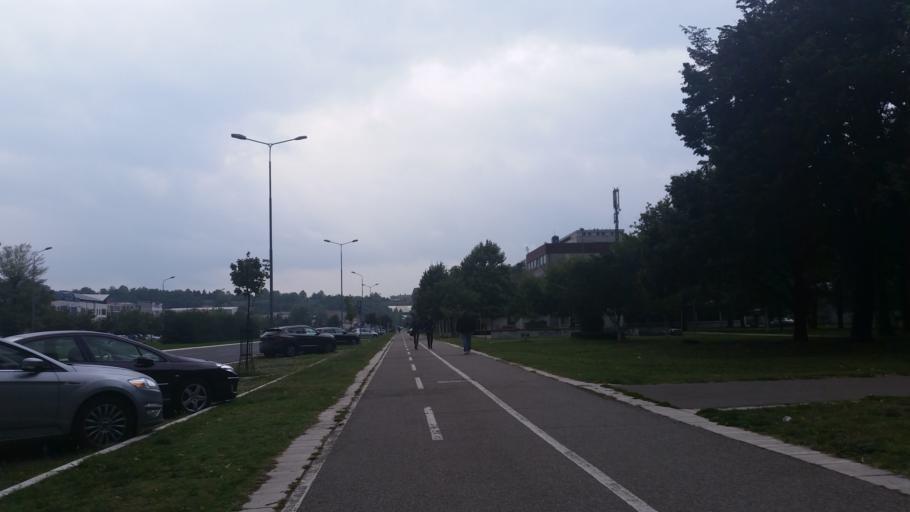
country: RS
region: Central Serbia
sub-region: Belgrade
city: Novi Beograd
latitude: 44.8162
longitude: 20.4029
